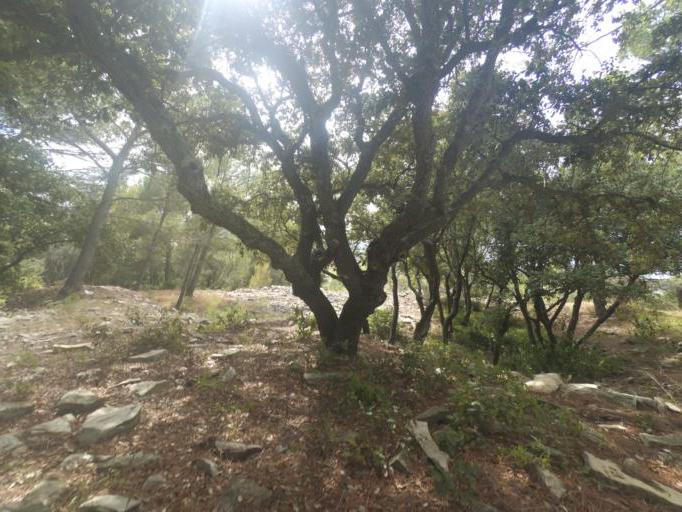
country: FR
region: Languedoc-Roussillon
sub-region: Departement du Gard
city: Nages-et-Solorgues
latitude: 43.7939
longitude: 4.2268
